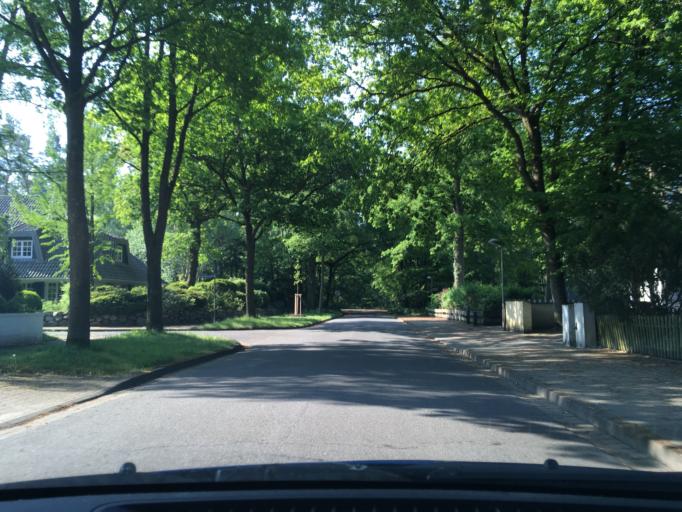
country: DE
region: Lower Saxony
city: Lueneburg
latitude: 53.2285
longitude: 10.4217
